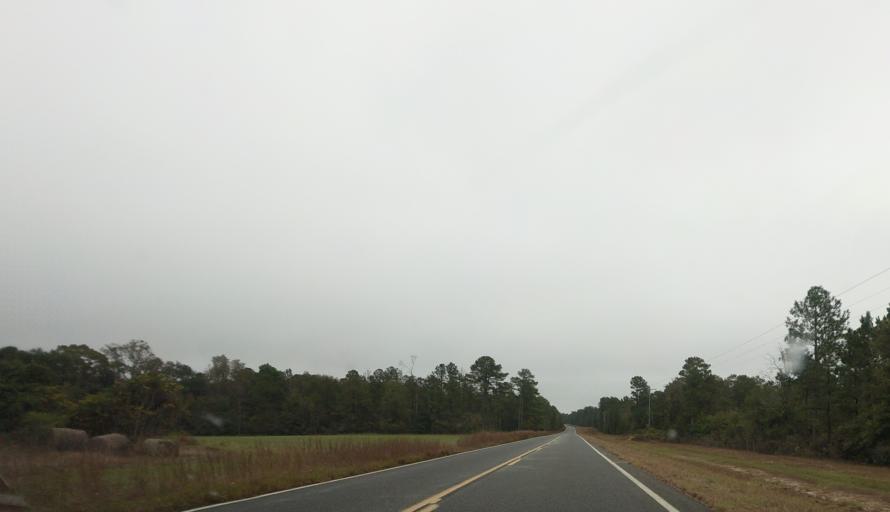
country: US
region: Georgia
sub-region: Taylor County
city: Butler
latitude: 32.4301
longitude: -84.3041
